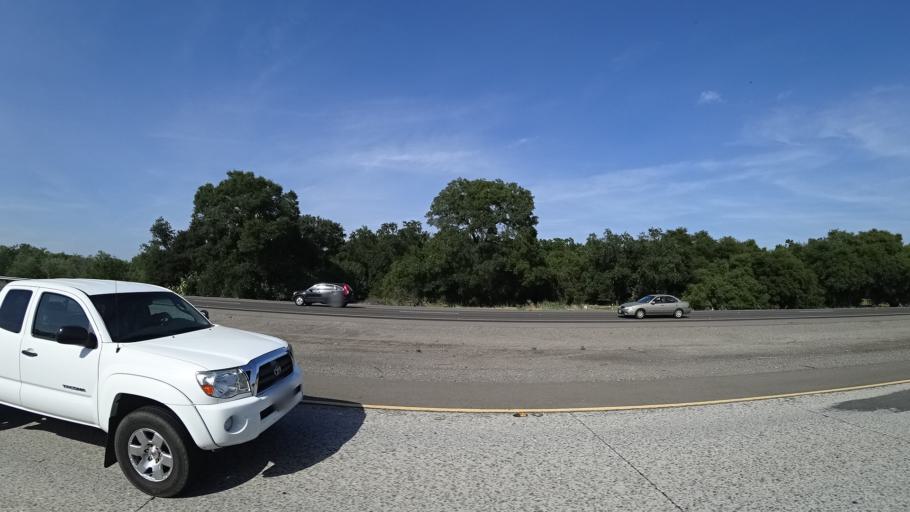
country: US
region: California
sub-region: Butte County
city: Durham
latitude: 39.6935
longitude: -121.7774
